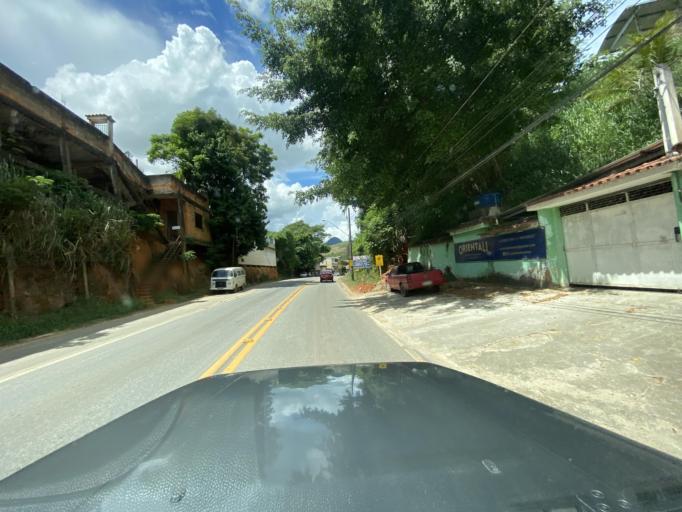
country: BR
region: Espirito Santo
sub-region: Jeronimo Monteiro
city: Jeronimo Monteiro
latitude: -20.7908
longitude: -41.3935
